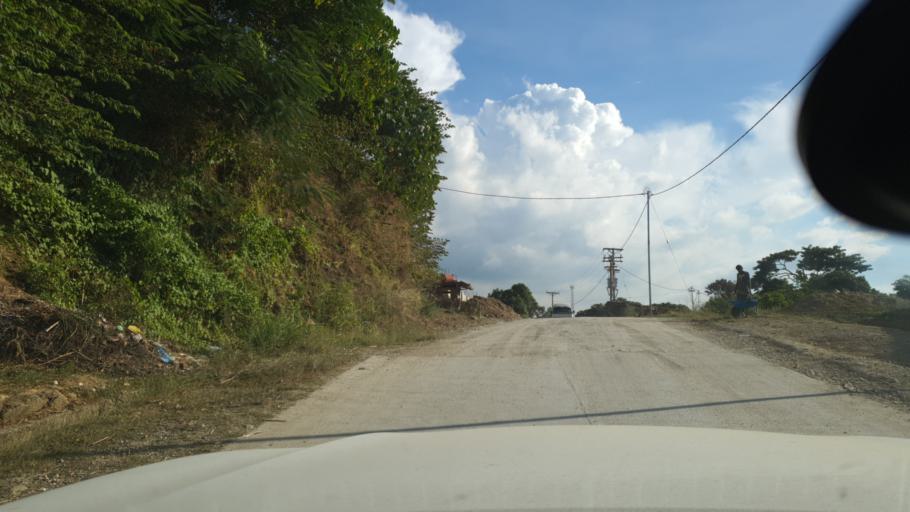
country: SB
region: Guadalcanal
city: Honiara
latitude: -9.4465
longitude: 159.9967
